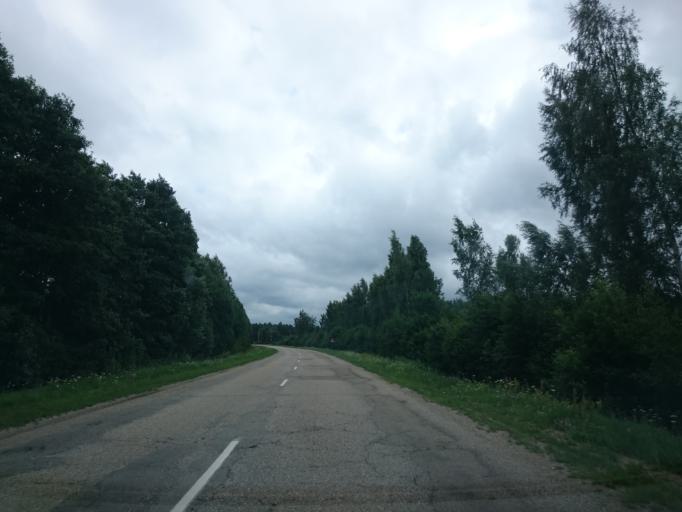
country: LV
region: Pavilostas
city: Pavilosta
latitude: 56.7979
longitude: 21.2323
